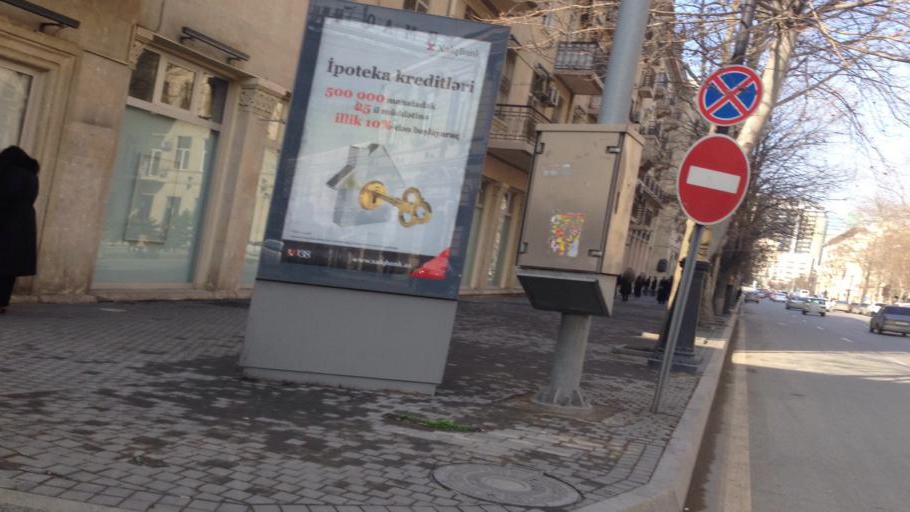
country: AZ
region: Baki
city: Badamdar
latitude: 40.3718
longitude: 49.8336
